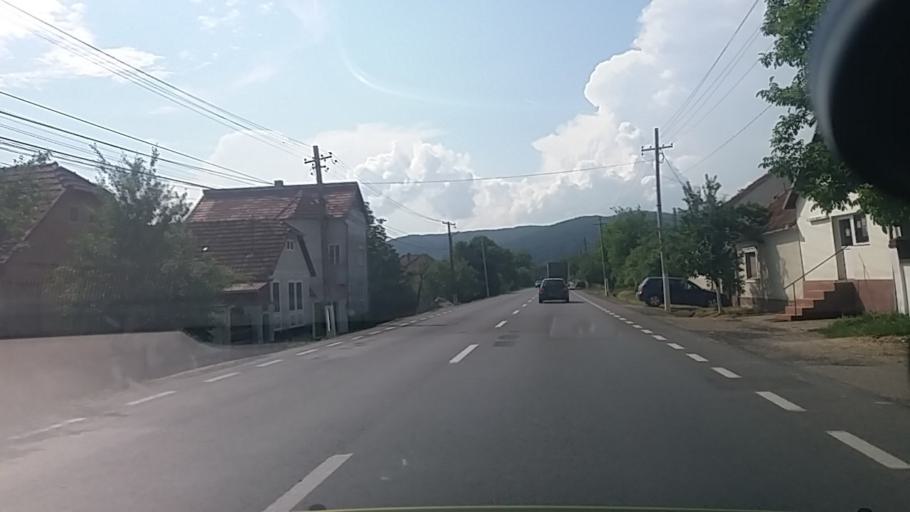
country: RO
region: Arad
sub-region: Comuna Barzava
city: Barzava
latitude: 46.1082
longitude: 21.9820
